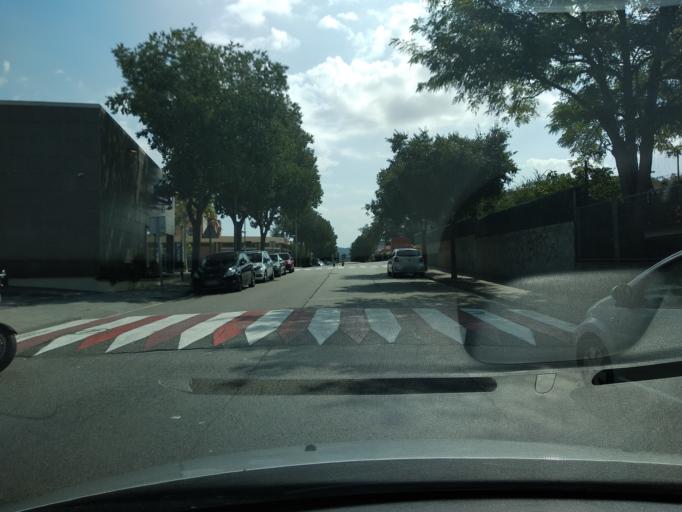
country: ES
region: Catalonia
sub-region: Provincia de Barcelona
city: Parets del Valles
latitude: 41.5652
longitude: 2.2264
